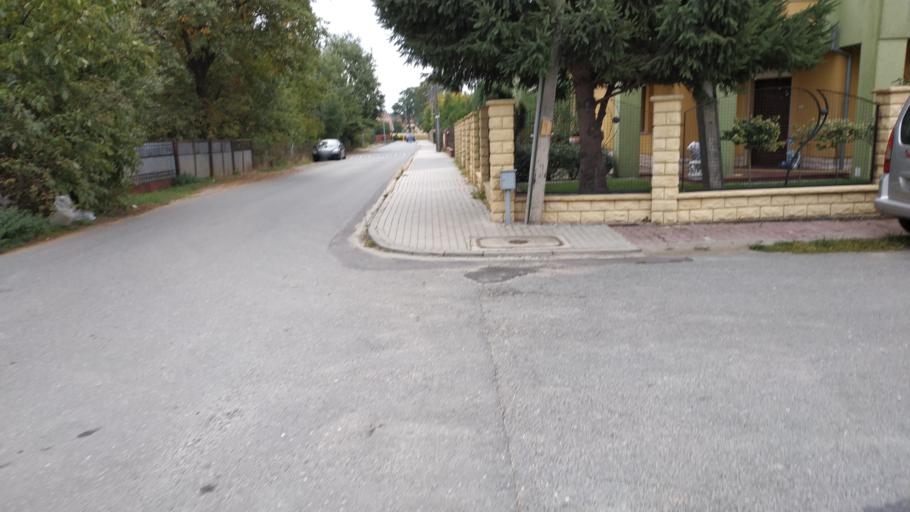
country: PL
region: Lower Silesian Voivodeship
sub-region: Powiat wroclawski
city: Tyniec Maly
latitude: 51.0203
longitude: 16.9150
